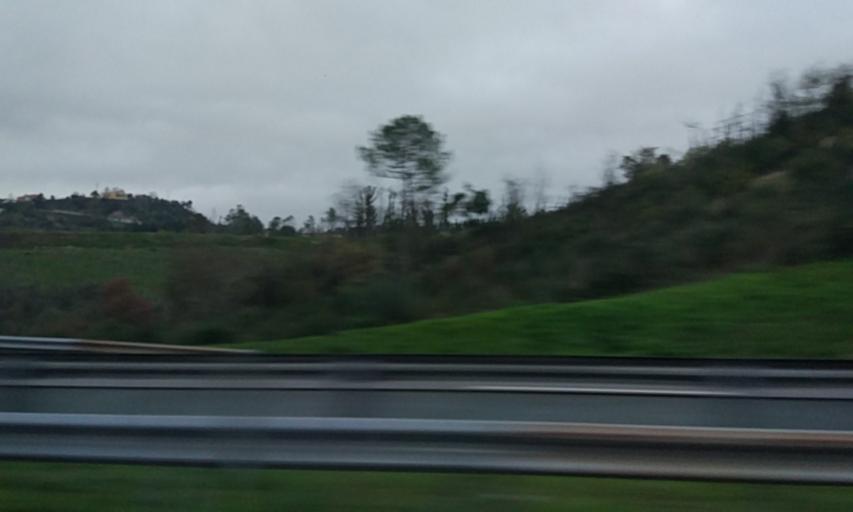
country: PT
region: Aveiro
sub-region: Mealhada
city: Pampilhosa do Botao
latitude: 40.2975
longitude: -8.4861
